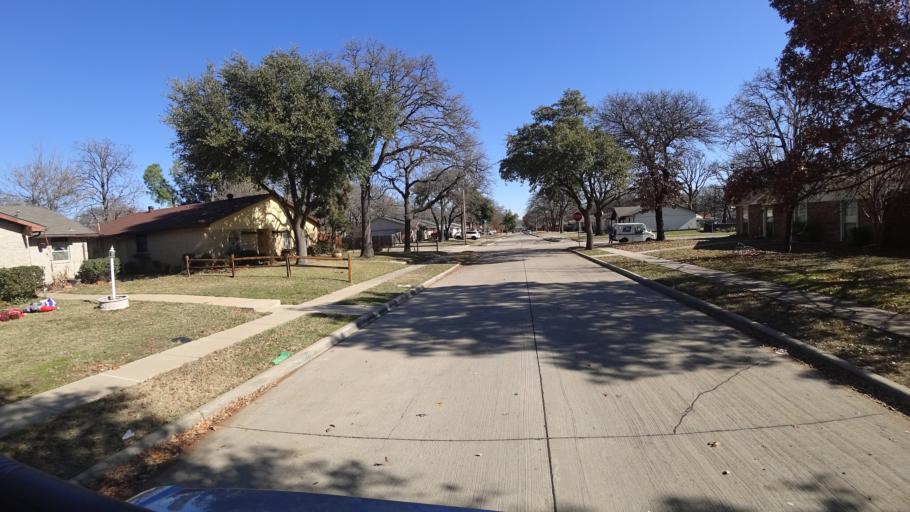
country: US
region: Texas
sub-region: Denton County
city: Lewisville
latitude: 33.0322
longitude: -97.0246
